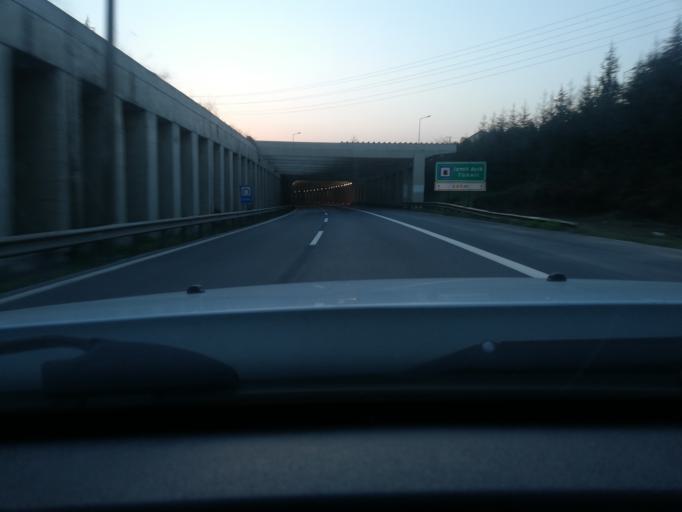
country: TR
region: Kocaeli
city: Derince
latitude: 40.7624
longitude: 29.8582
